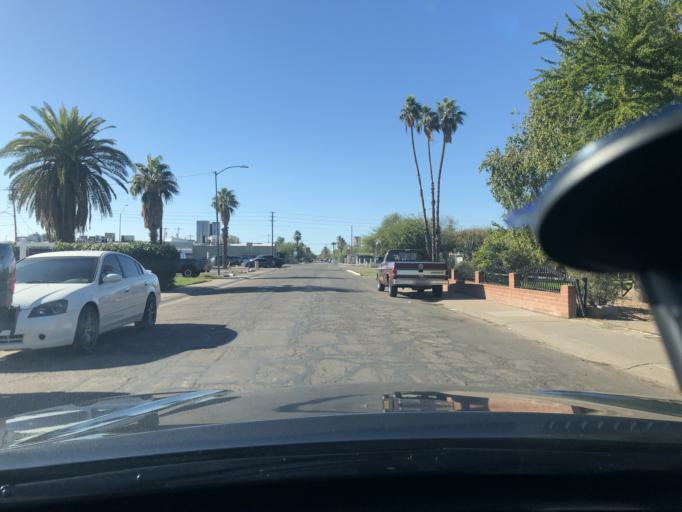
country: US
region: Arizona
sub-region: Maricopa County
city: Phoenix
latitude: 33.4667
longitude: -112.0463
